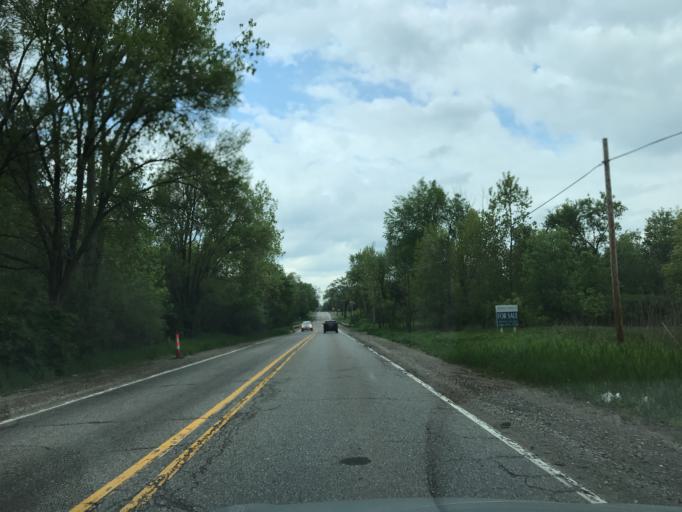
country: US
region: Michigan
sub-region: Oakland County
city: South Lyon
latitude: 42.4875
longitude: -83.6531
